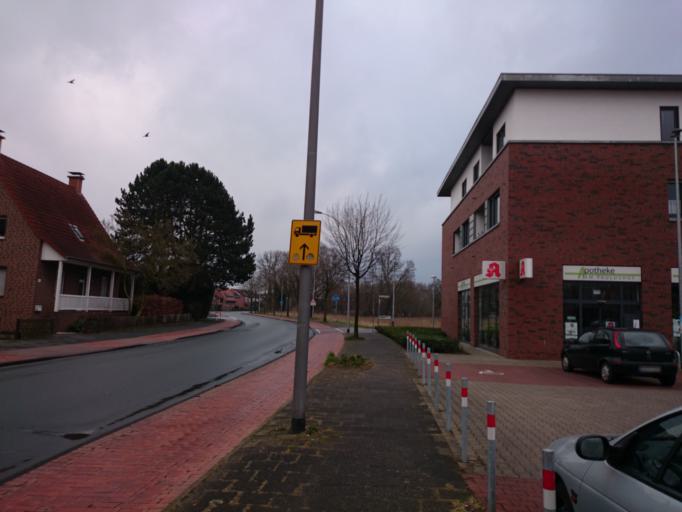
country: DE
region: North Rhine-Westphalia
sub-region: Regierungsbezirk Munster
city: Muenster
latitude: 51.9297
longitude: 7.5812
